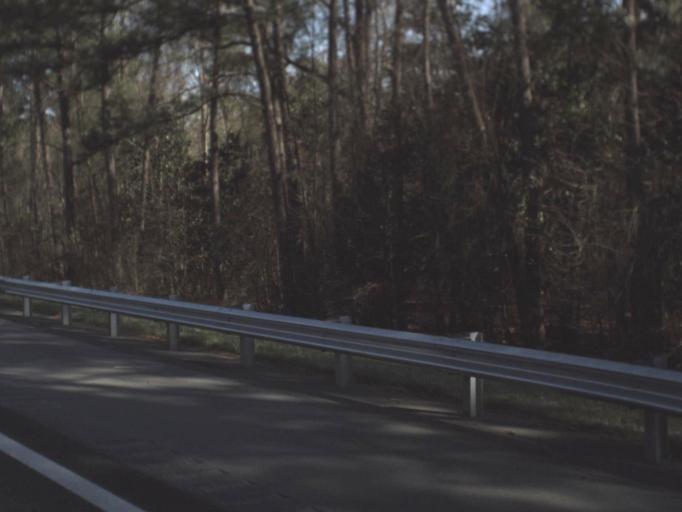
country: US
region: Florida
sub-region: Gadsden County
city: Chattahoochee
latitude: 30.6222
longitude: -84.7969
